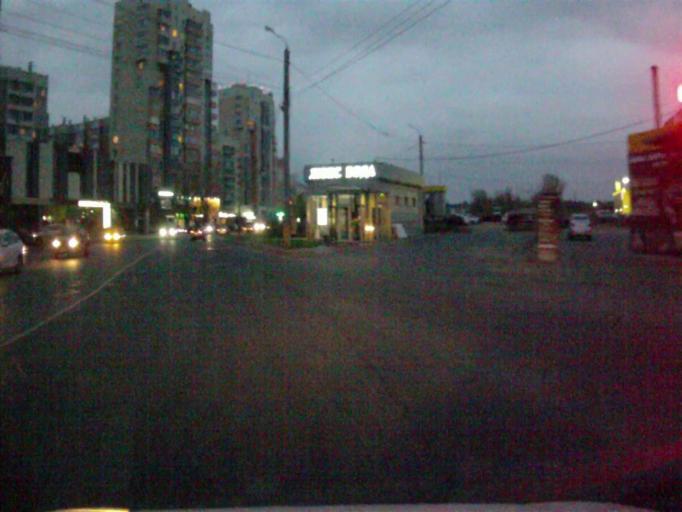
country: RU
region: Chelyabinsk
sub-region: Gorod Chelyabinsk
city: Chelyabinsk
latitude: 55.1624
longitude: 61.2950
